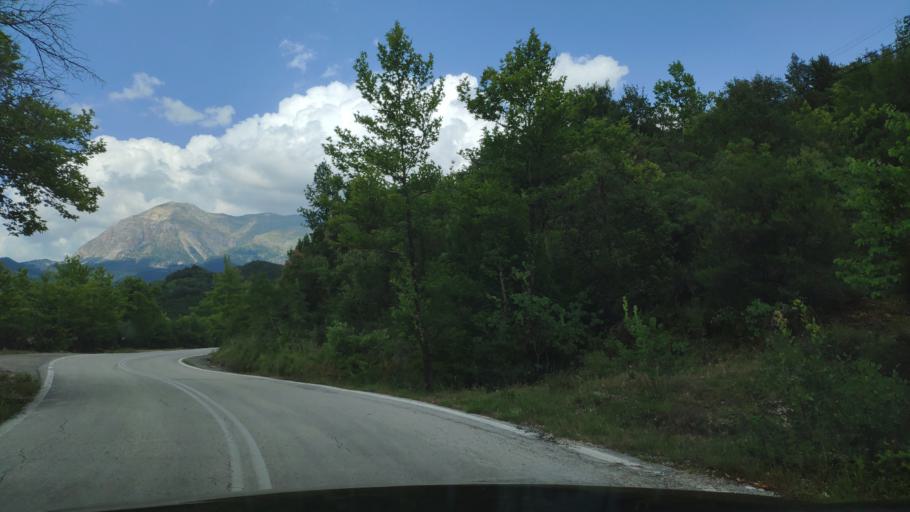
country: GR
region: Epirus
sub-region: Nomos Artas
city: Agios Dimitrios
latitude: 39.4577
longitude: 21.0561
